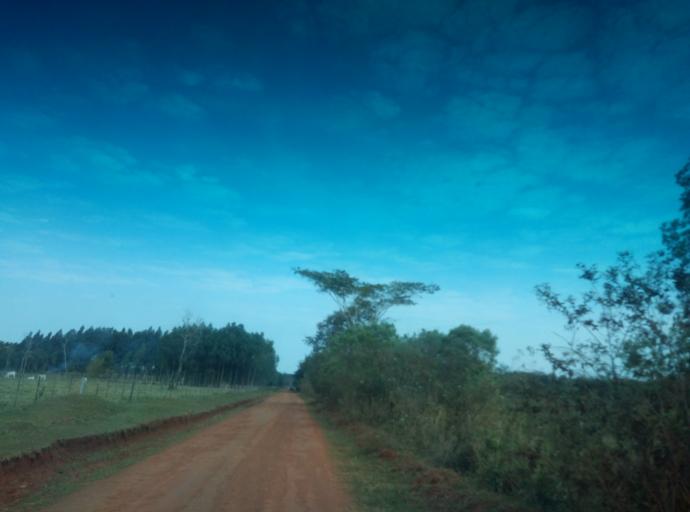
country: PY
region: Caaguazu
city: Carayao
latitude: -25.1930
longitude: -56.2520
